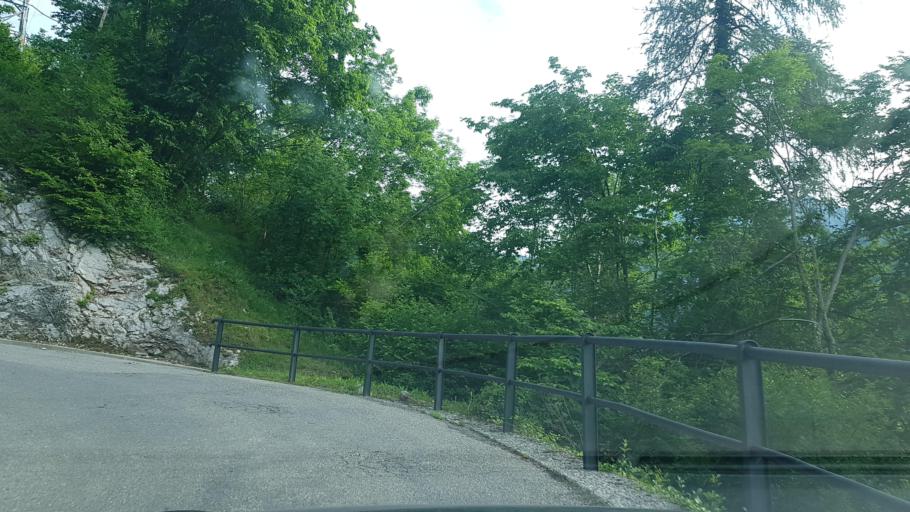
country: IT
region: Friuli Venezia Giulia
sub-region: Provincia di Udine
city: Zuglio
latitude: 46.4680
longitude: 13.0199
